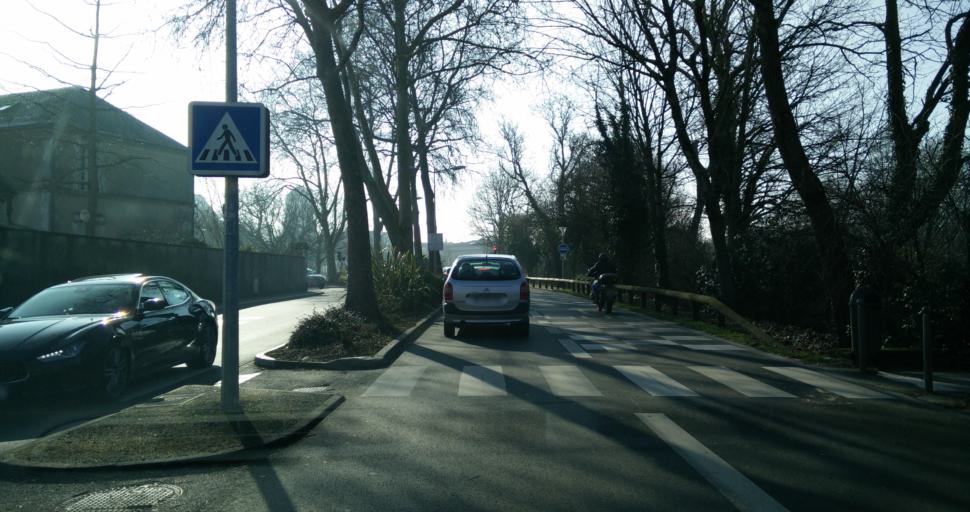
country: FR
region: Poitou-Charentes
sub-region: Departement de la Charente-Maritime
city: La Rochelle
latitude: 46.1637
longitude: -1.1554
